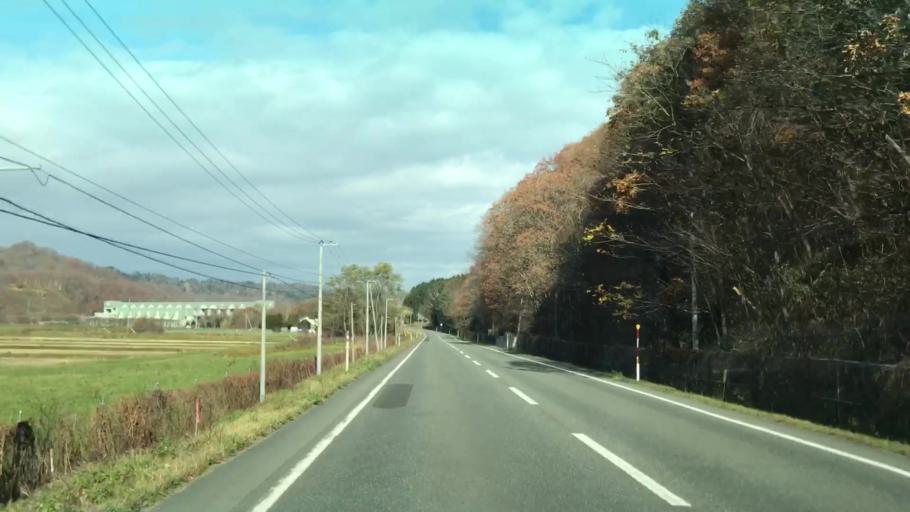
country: JP
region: Hokkaido
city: Shizunai-furukawacho
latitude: 42.6206
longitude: 142.1505
